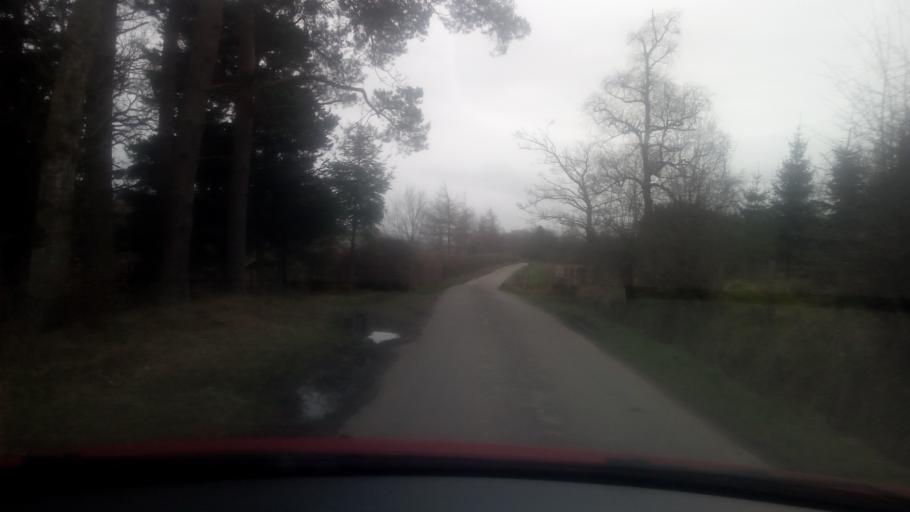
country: GB
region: Scotland
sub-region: The Scottish Borders
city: Jedburgh
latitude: 55.4382
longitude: -2.6408
